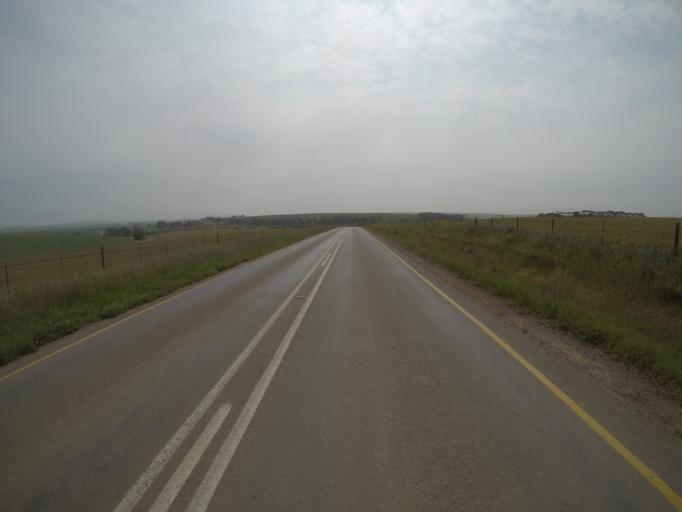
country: ZA
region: Western Cape
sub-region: City of Cape Town
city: Kraaifontein
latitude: -33.7345
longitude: 18.6337
